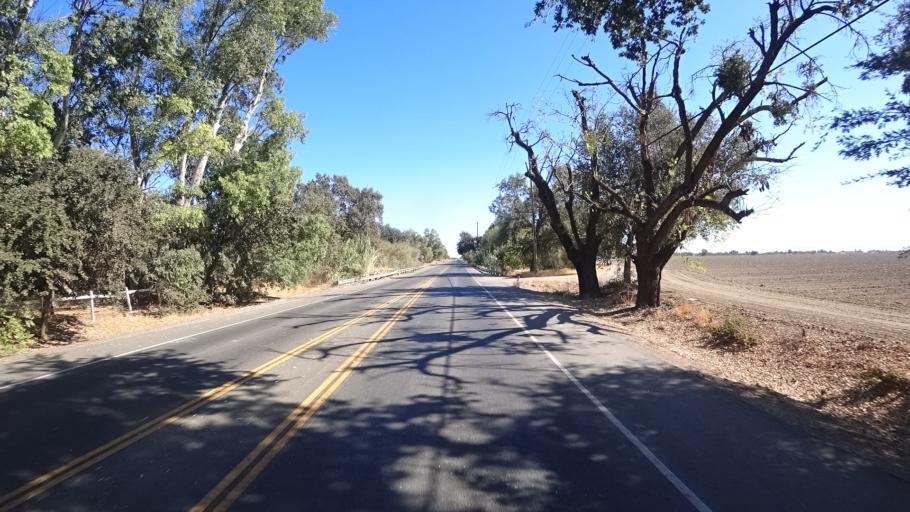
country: US
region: California
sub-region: Yolo County
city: Davis
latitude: 38.5615
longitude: -121.8572
